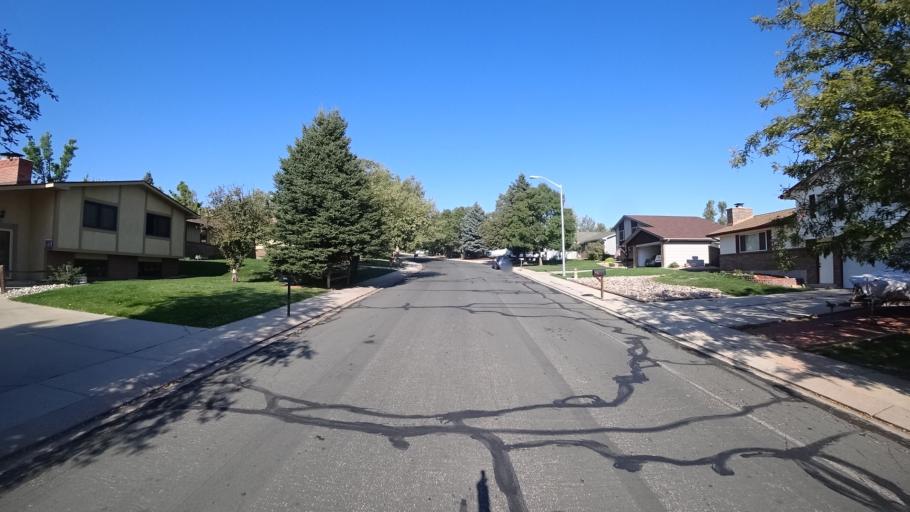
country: US
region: Colorado
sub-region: El Paso County
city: Cimarron Hills
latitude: 38.8801
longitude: -104.7247
